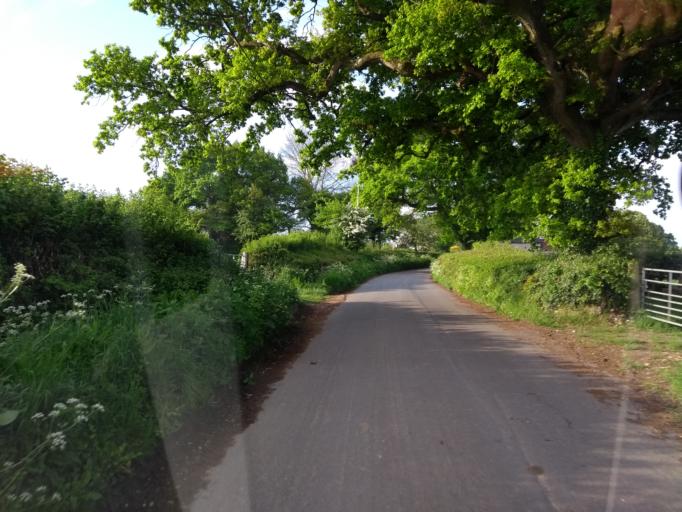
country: GB
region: England
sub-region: Devon
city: Axminster
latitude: 50.8082
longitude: -2.9515
